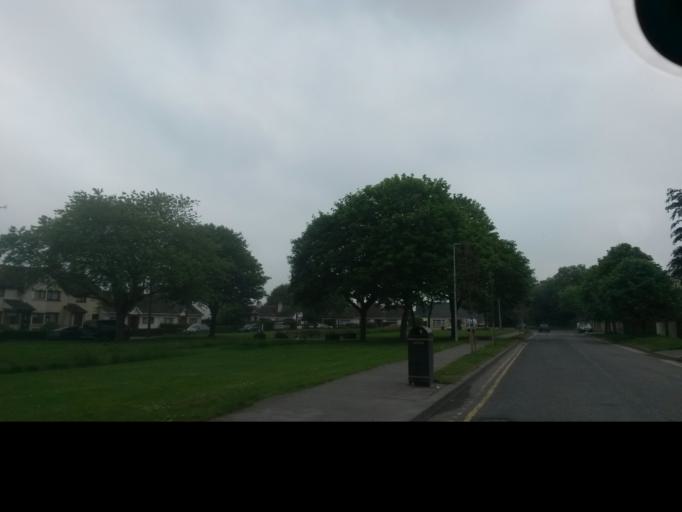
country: IE
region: Leinster
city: Donabate
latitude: 53.4852
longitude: -6.1493
